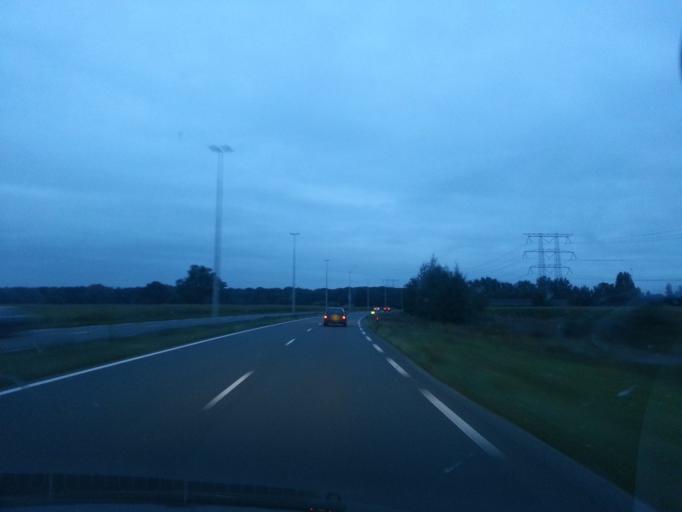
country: NL
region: North Brabant
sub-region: Gemeente Tilburg
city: Tilburg
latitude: 51.5921
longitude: 5.1067
